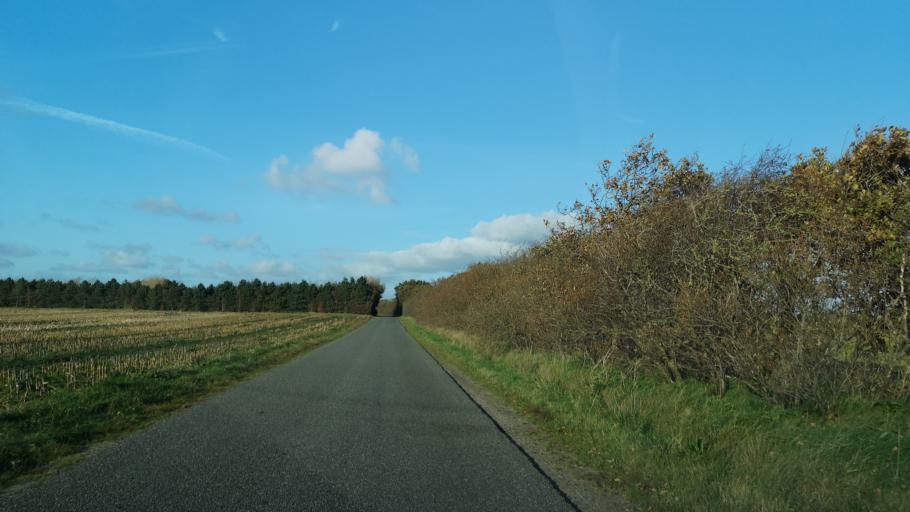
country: DK
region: Central Jutland
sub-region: Ringkobing-Skjern Kommune
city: Skjern
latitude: 55.8519
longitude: 8.3494
